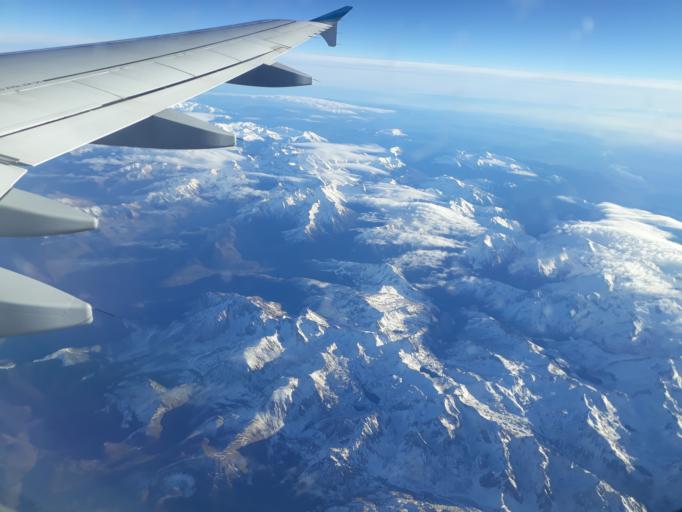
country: FR
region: Midi-Pyrenees
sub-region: Departement des Hautes-Pyrenees
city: Campan
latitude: 42.9977
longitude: 0.1330
